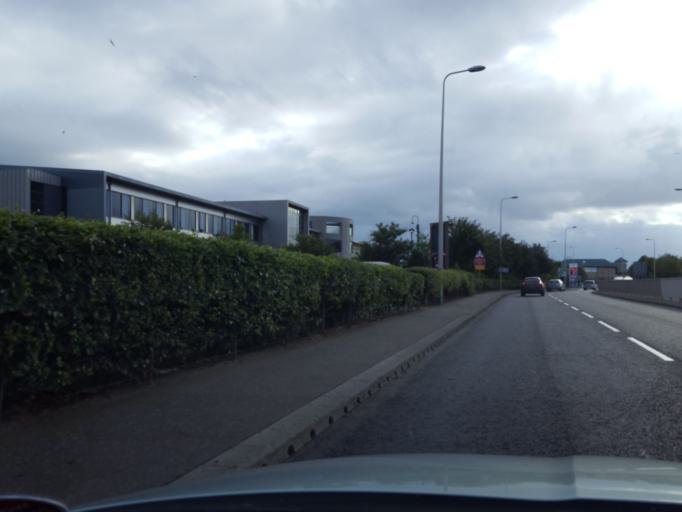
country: GB
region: Scotland
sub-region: Dundee City
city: Dundee
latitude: 56.4561
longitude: -2.9710
